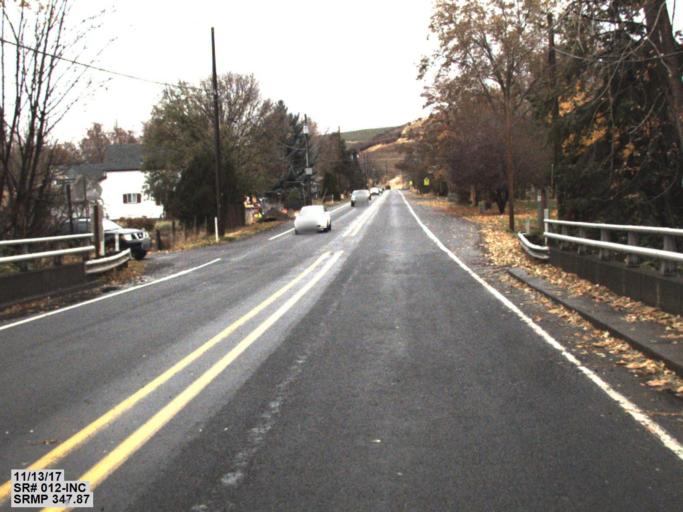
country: US
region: Washington
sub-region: Walla Walla County
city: Waitsburg
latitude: 46.1404
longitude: -118.1545
